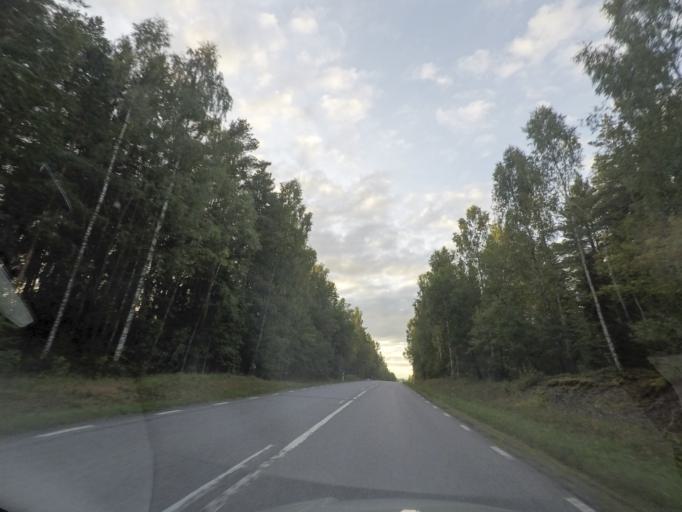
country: SE
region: OErebro
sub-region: Hallefors Kommun
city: Haellefors
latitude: 59.7154
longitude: 14.5296
